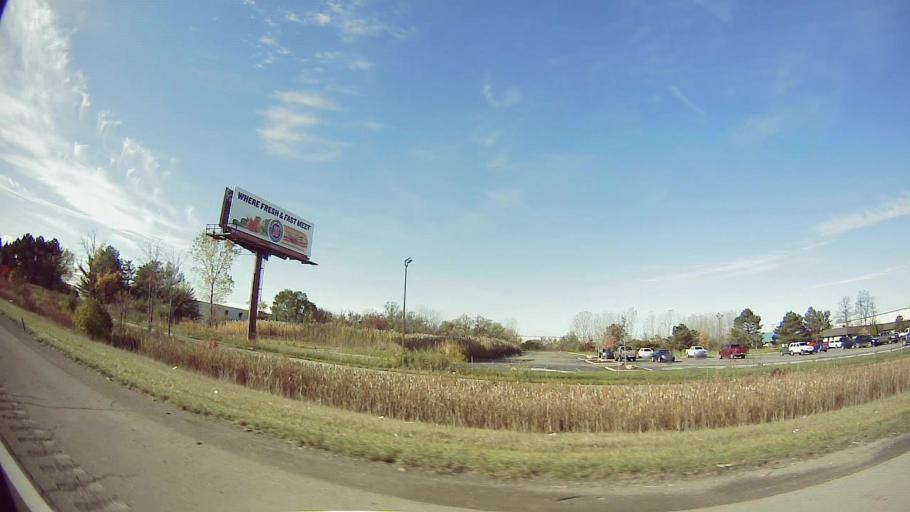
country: US
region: Michigan
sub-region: Wayne County
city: Romulus
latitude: 42.2411
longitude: -83.4401
